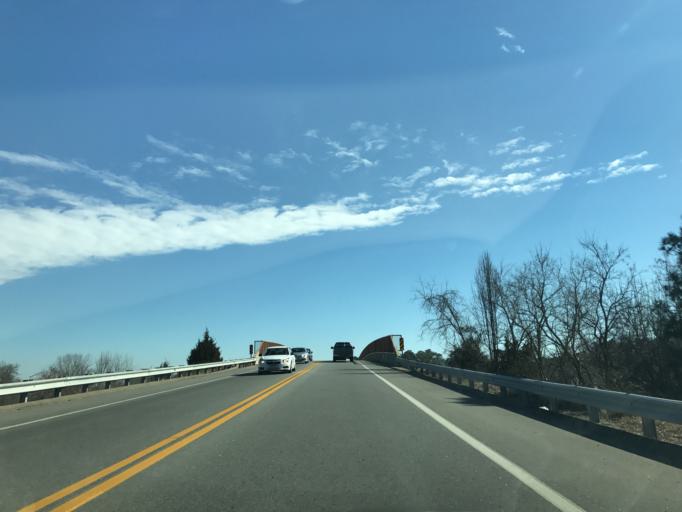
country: US
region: Maryland
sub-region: Queen Anne's County
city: Chester
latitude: 38.9765
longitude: -76.2851
